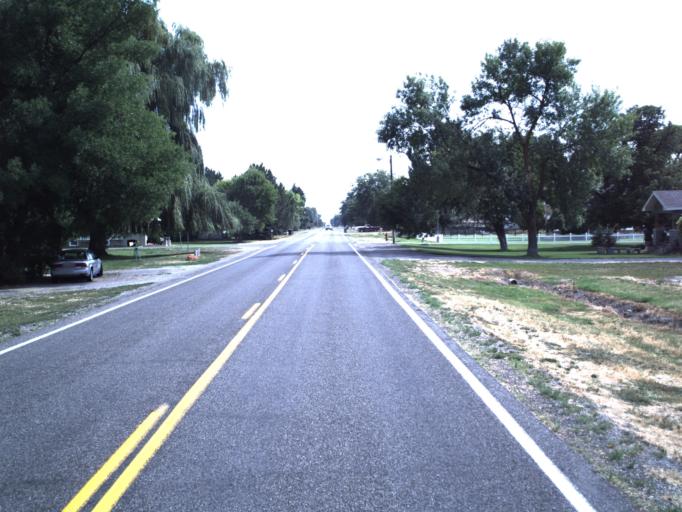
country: US
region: Utah
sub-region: Box Elder County
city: Garland
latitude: 41.8121
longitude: -112.1161
